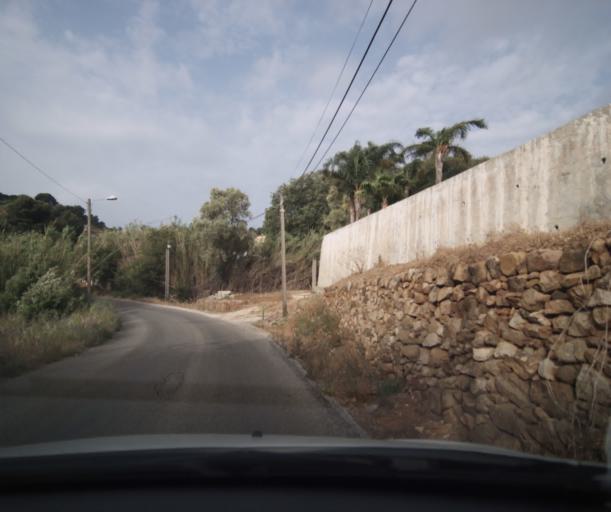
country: FR
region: Provence-Alpes-Cote d'Azur
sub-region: Departement du Var
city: Carqueiranne
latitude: 43.0850
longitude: 6.0522
